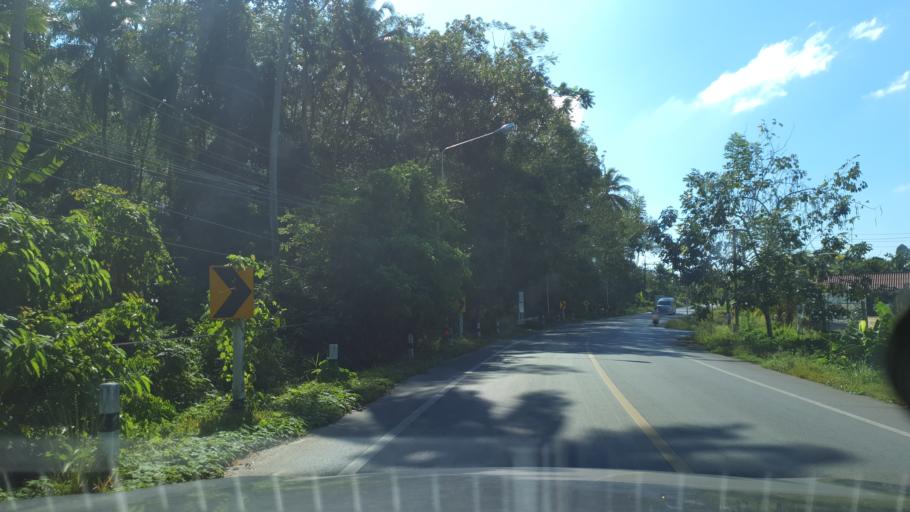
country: TH
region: Phangnga
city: Ban Ao Nang
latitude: 8.0701
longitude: 98.8087
